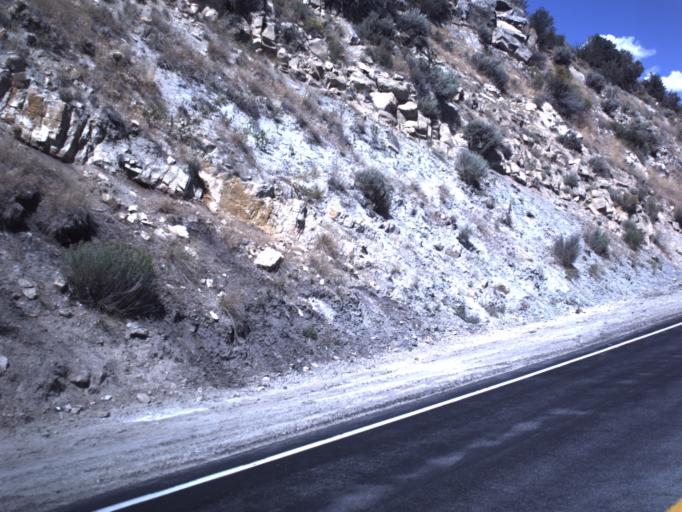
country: US
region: Utah
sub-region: Summit County
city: Oakley
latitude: 40.7846
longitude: -111.4089
